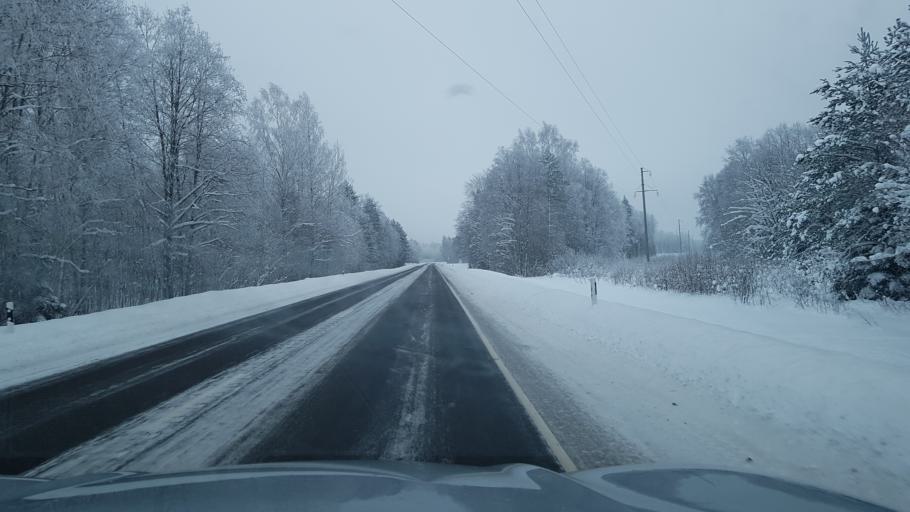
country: EE
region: Ida-Virumaa
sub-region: Johvi vald
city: Johvi
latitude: 59.2993
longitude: 27.3963
